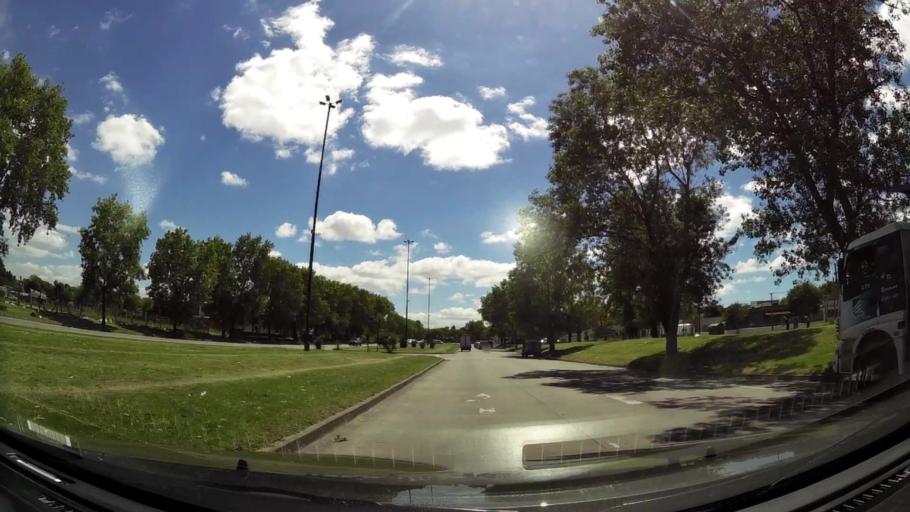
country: UY
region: Montevideo
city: Montevideo
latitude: -34.8597
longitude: -56.1450
